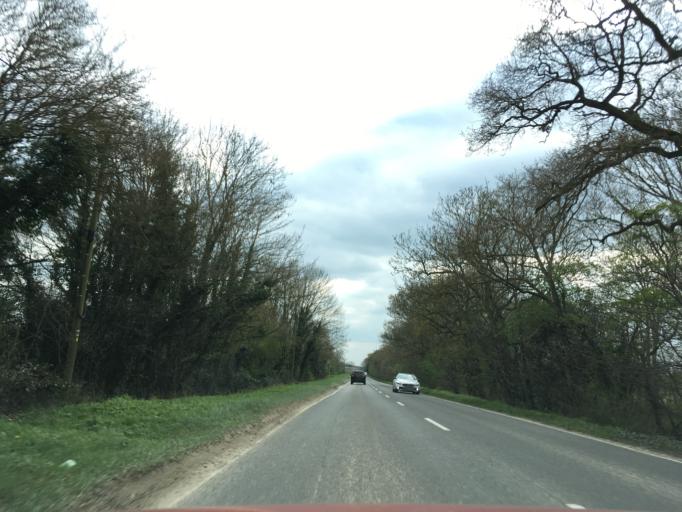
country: GB
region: England
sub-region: Oxfordshire
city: Woodstock
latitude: 51.8415
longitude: -1.3307
